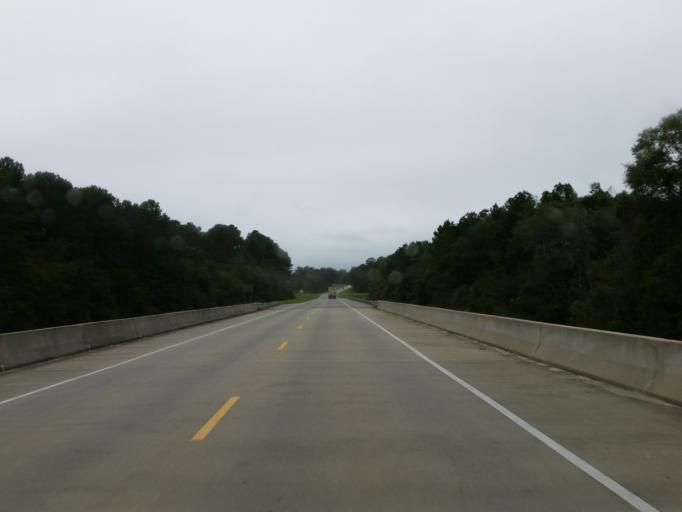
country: US
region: Georgia
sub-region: Cook County
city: Adel
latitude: 31.1226
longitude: -83.3263
